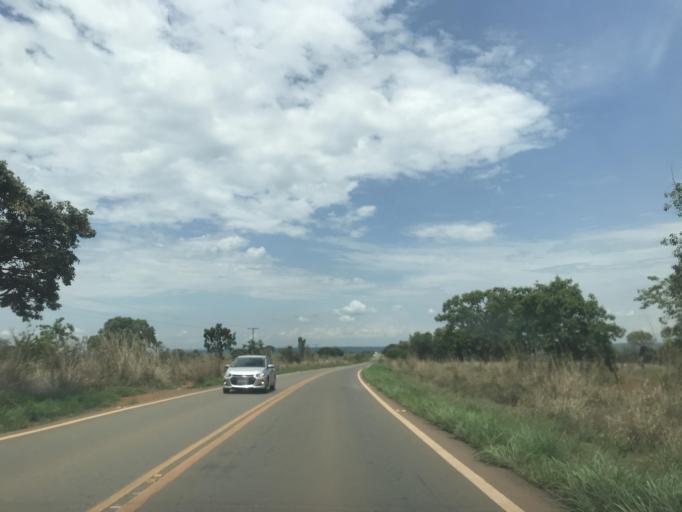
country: BR
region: Goias
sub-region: Luziania
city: Luziania
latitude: -16.3479
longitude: -48.0258
